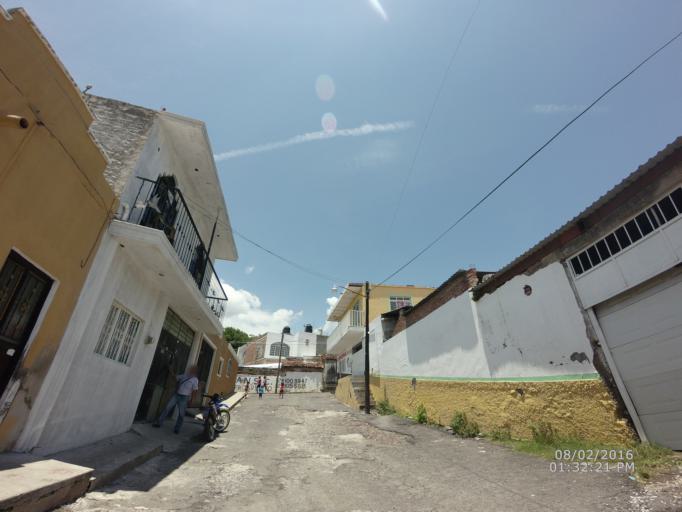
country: MX
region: Nayarit
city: Ixtlan del Rio
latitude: 21.0348
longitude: -104.3629
